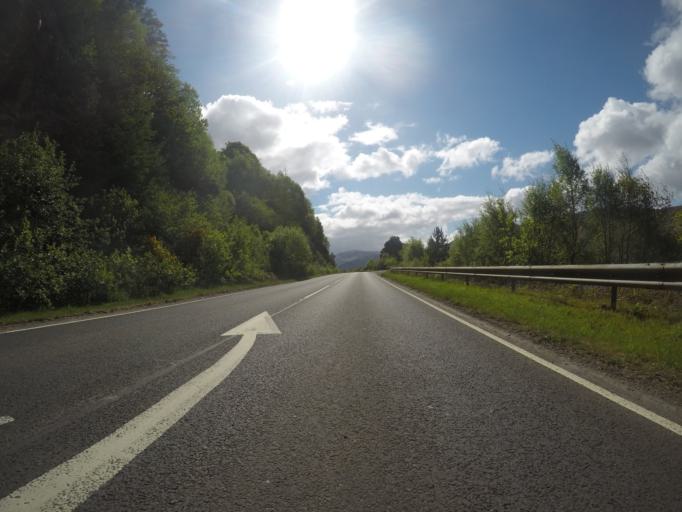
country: GB
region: Scotland
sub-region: Highland
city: Fort William
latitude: 57.2710
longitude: -5.5092
